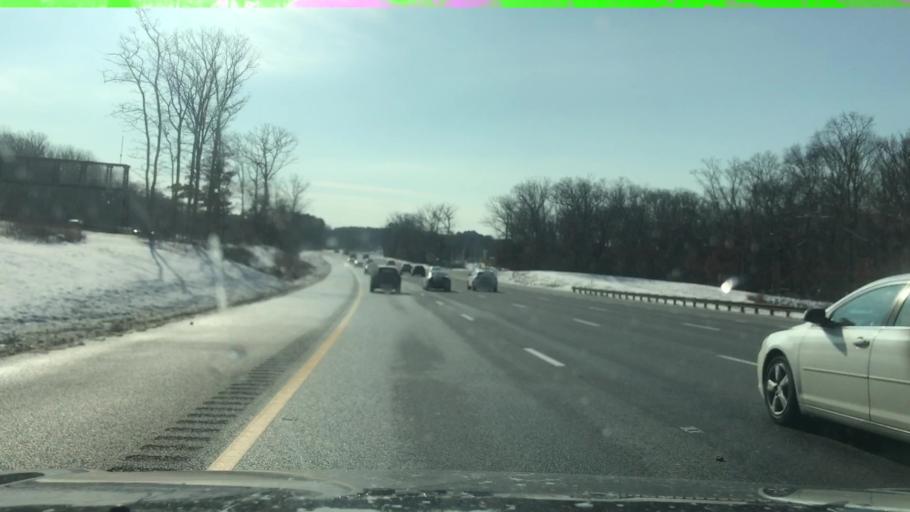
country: US
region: New Jersey
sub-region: Monmouth County
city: Ramtown
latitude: 40.1254
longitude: -74.1265
